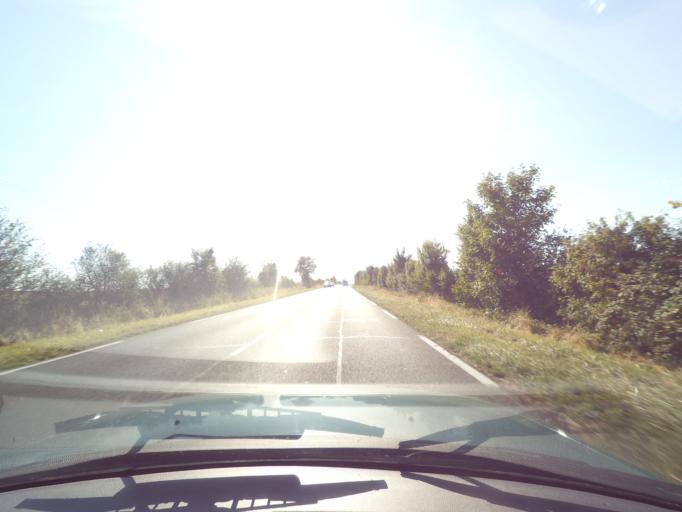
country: FR
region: Poitou-Charentes
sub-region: Departement de la Vienne
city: Ayron
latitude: 46.6568
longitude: 0.0979
